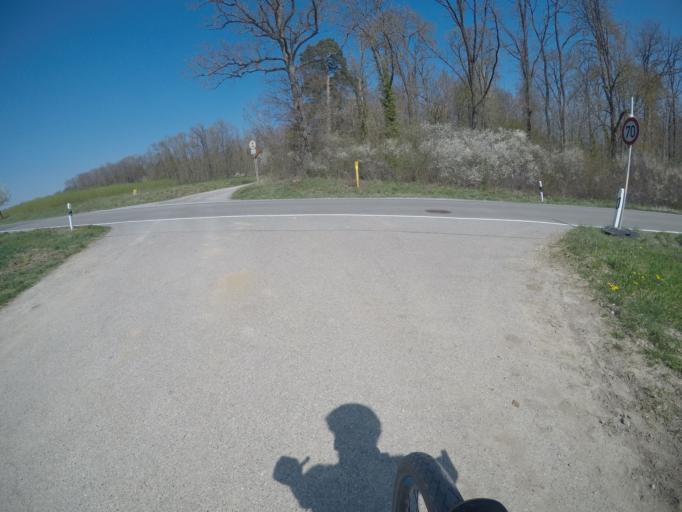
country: DE
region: Baden-Wuerttemberg
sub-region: Regierungsbezirk Stuttgart
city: Renningen
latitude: 48.7448
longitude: 8.9291
